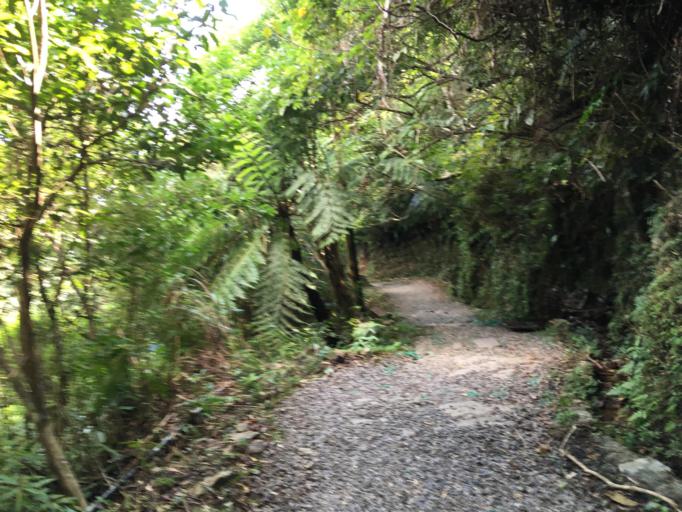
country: TW
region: Taiwan
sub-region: Yilan
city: Yilan
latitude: 24.8453
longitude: 121.7765
